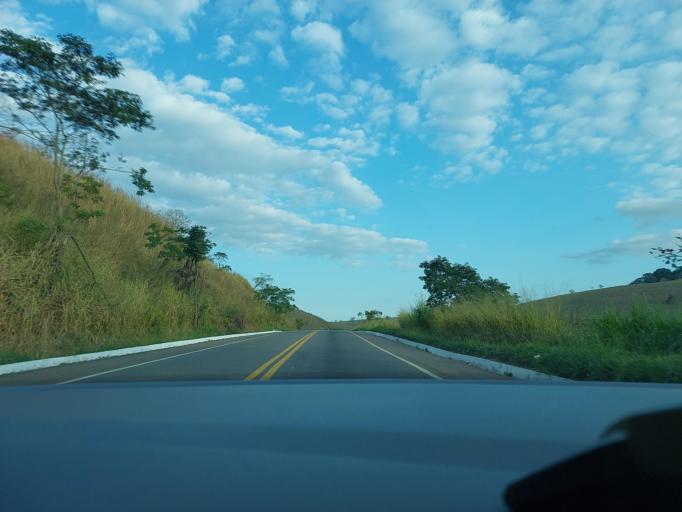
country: BR
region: Minas Gerais
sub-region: Muriae
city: Muriae
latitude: -21.1327
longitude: -42.3168
